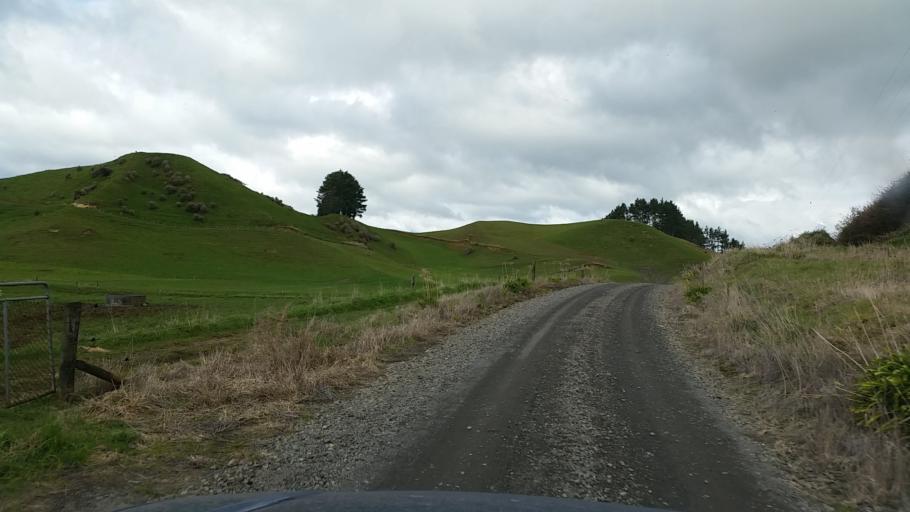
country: NZ
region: Taranaki
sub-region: South Taranaki District
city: Eltham
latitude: -39.3521
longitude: 174.3842
